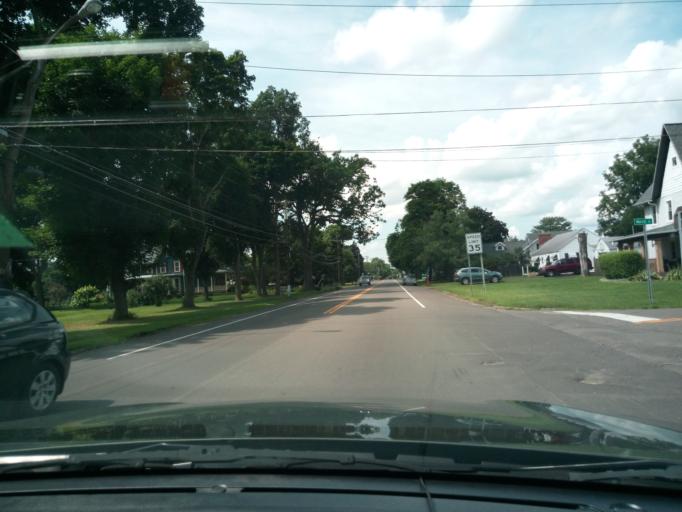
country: US
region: New York
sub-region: Chemung County
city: Southport
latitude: 42.0584
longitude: -76.7828
